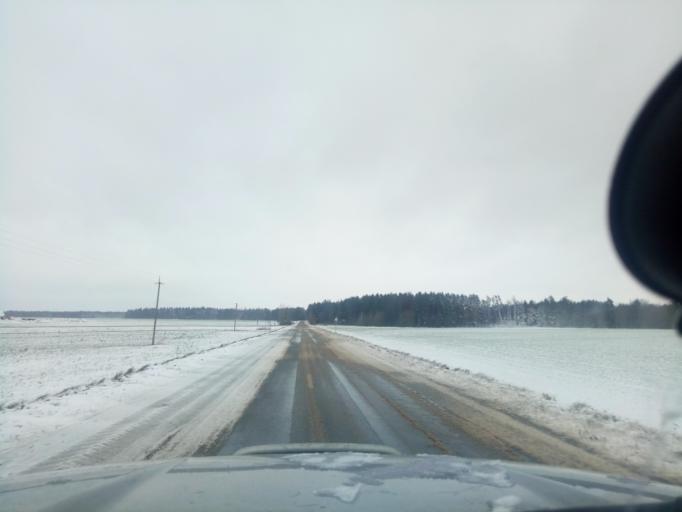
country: BY
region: Minsk
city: Tsimkavichy
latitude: 53.0475
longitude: 26.8640
